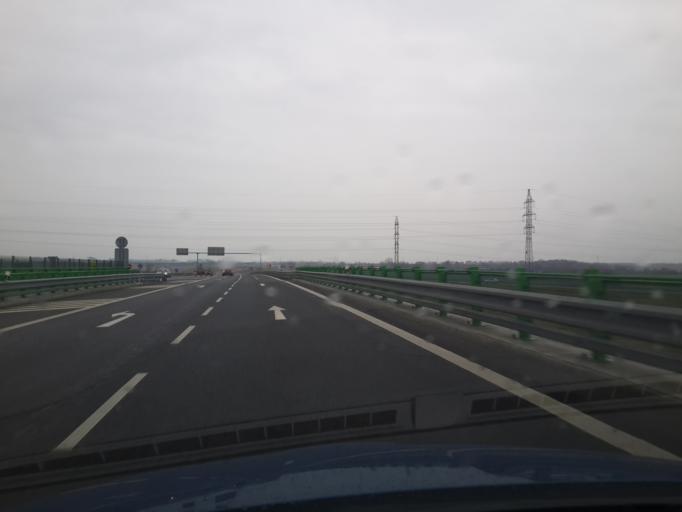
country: SK
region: Bratislavsky
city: Stupava
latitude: 48.2492
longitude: 17.0129
